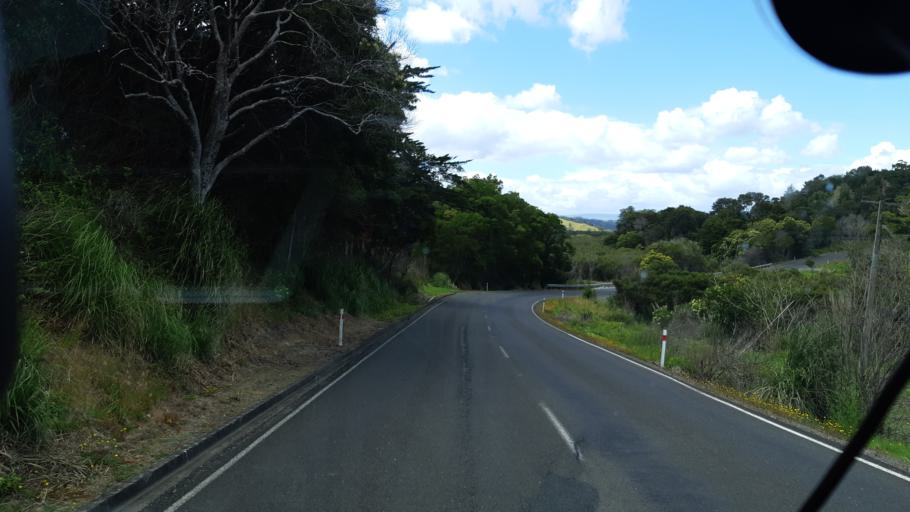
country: NZ
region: Northland
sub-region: Far North District
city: Taipa
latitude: -35.2660
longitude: 173.5245
